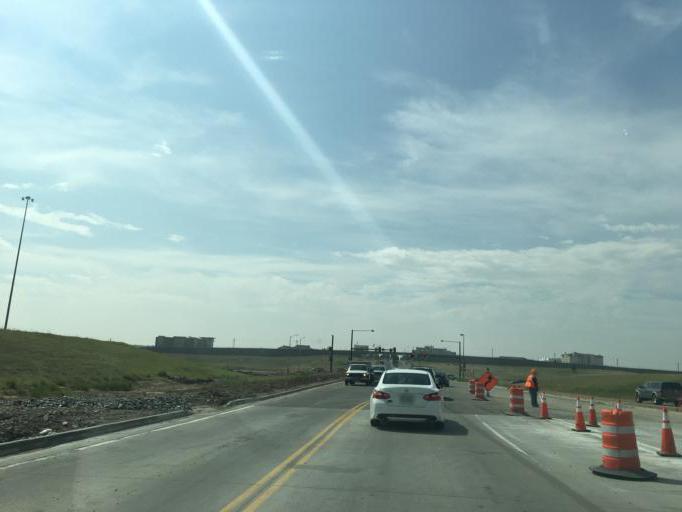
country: US
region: Colorado
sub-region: Adams County
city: Aurora
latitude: 39.8326
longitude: -104.7719
